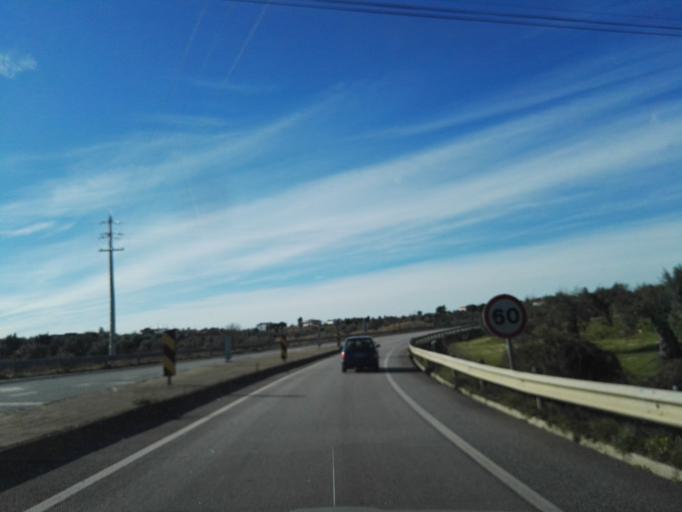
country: PT
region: Santarem
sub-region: Abrantes
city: Alferrarede
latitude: 39.4763
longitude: -8.0822
